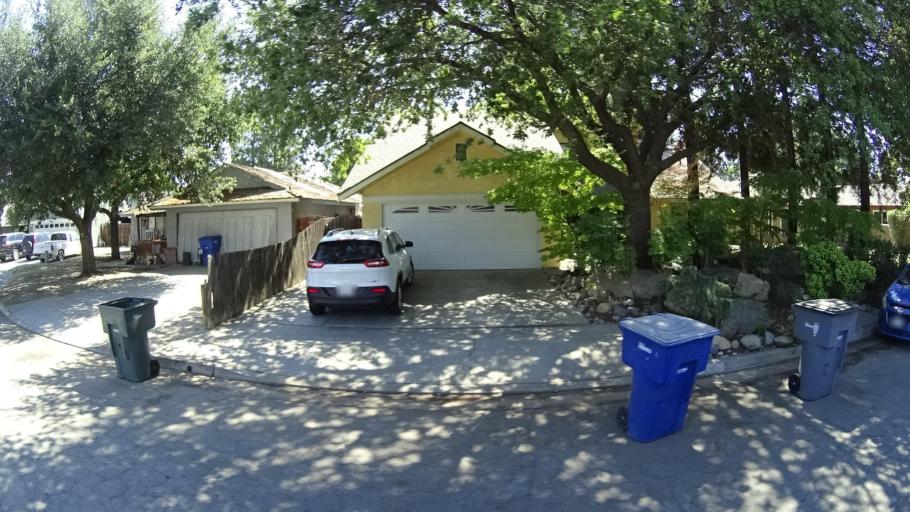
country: US
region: California
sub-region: Fresno County
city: Sunnyside
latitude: 36.7493
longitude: -119.6902
